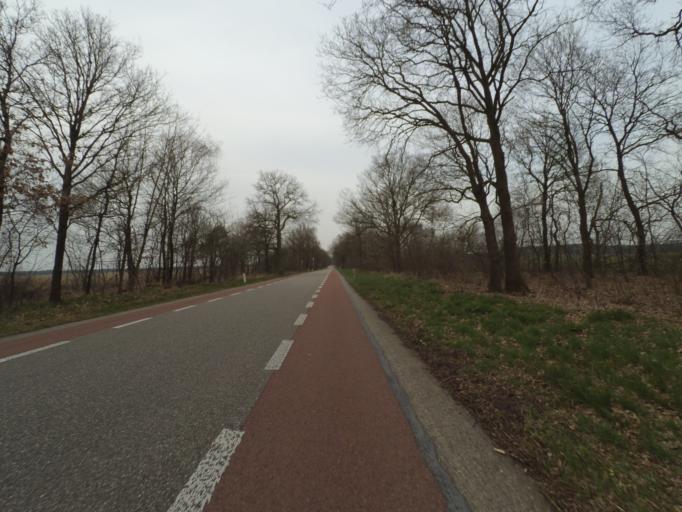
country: NL
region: Gelderland
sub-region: Gemeente Arnhem
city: Hoogkamp
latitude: 52.0874
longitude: 5.8794
